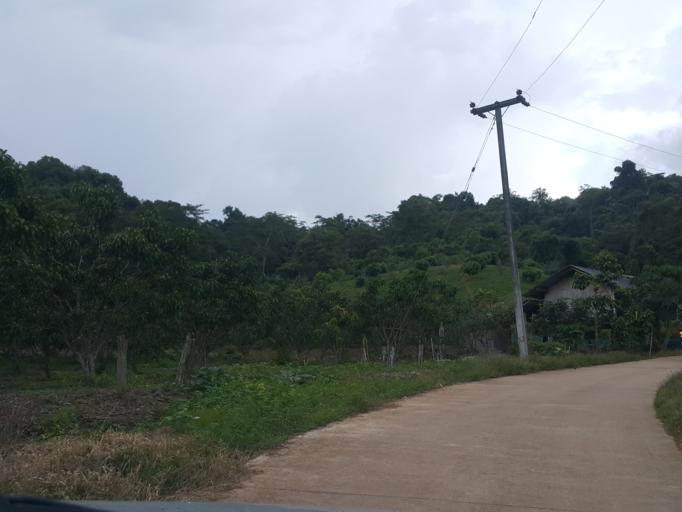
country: TH
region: Chiang Mai
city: Phrao
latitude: 19.3240
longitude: 99.1330
